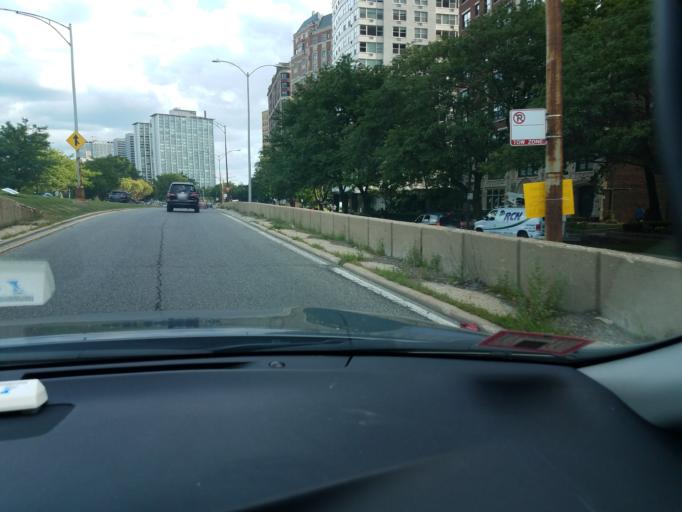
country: US
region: Illinois
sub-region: Cook County
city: Evanston
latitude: 41.9542
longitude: -87.6450
